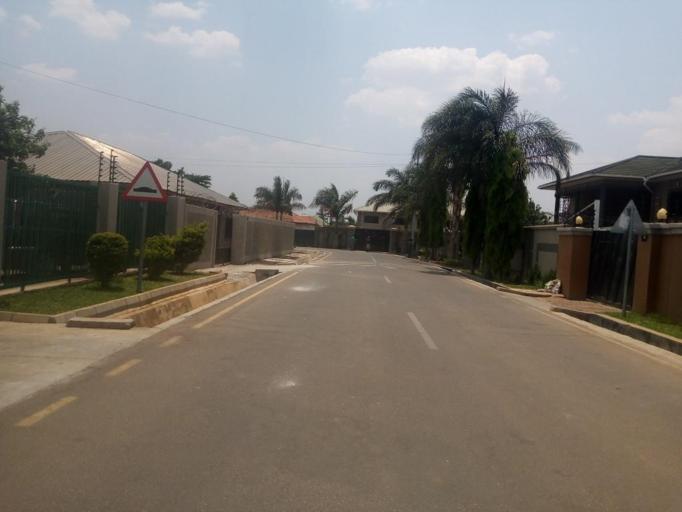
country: ZM
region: Lusaka
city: Lusaka
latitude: -15.3978
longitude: 28.3919
